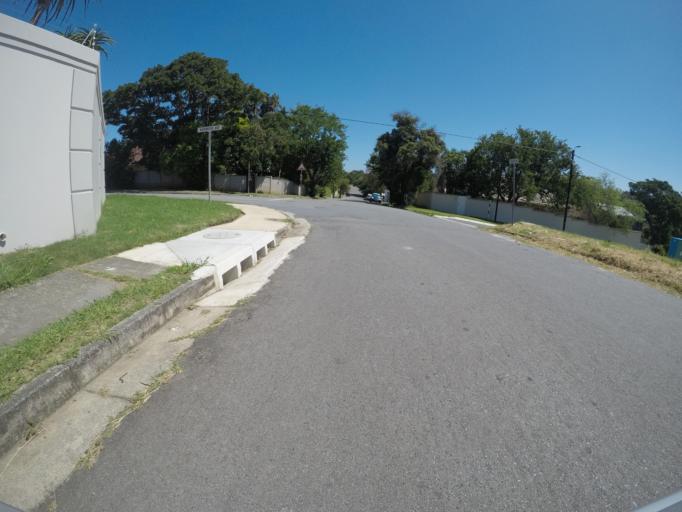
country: ZA
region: Eastern Cape
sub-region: Buffalo City Metropolitan Municipality
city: East London
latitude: -32.9793
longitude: 27.9223
